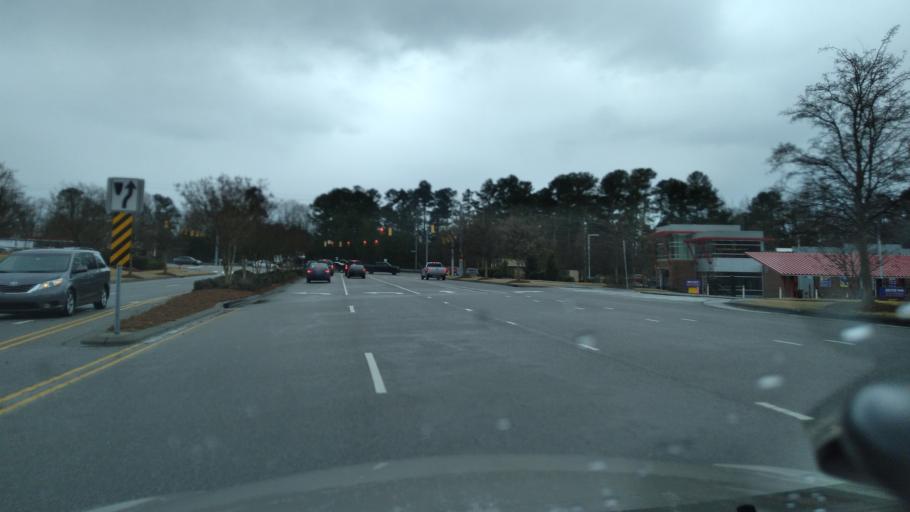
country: US
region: North Carolina
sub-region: Wake County
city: Knightdale
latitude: 35.7963
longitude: -78.5209
